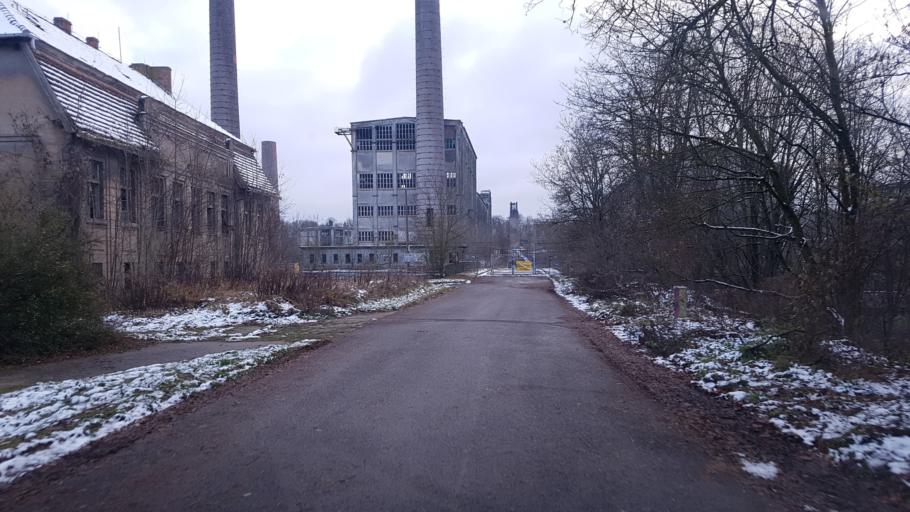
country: DE
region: Brandenburg
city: Petershagen
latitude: 52.4863
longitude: 13.7896
